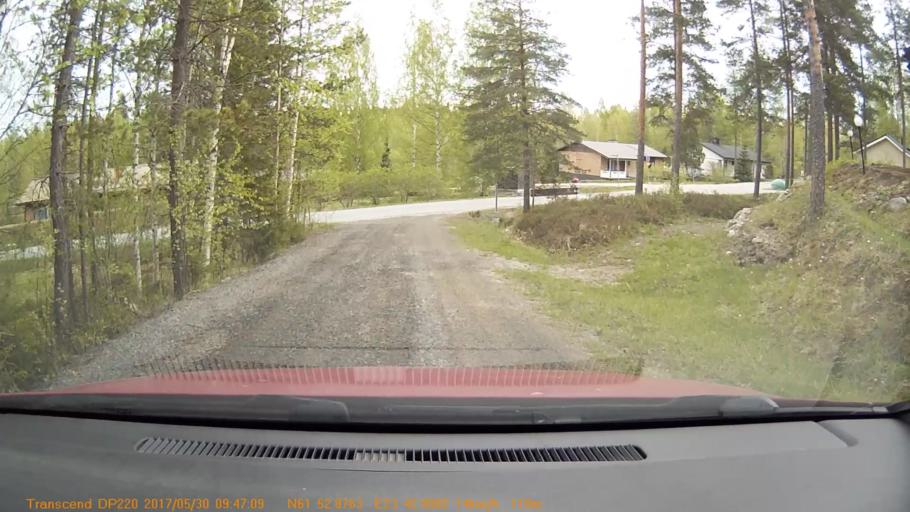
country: FI
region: Pirkanmaa
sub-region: Tampere
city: Kuru
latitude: 61.8813
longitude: 23.7151
